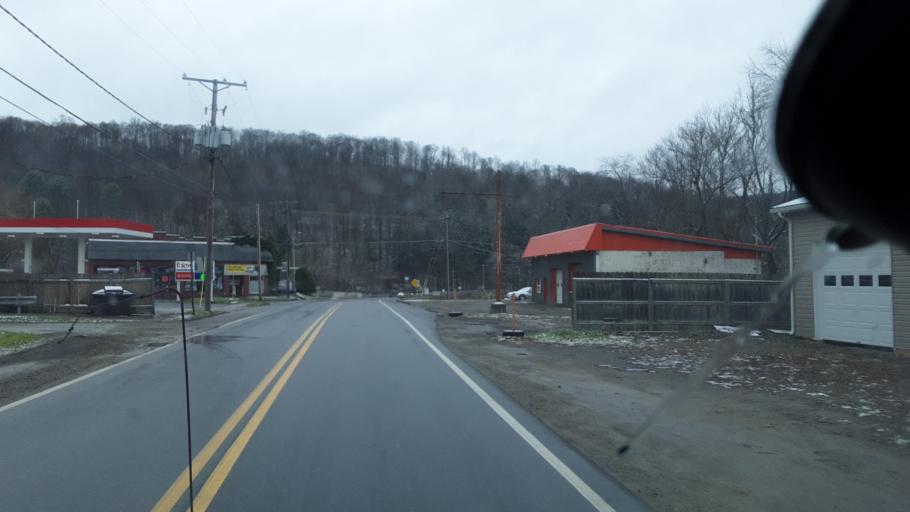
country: US
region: Pennsylvania
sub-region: Potter County
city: Shinglehouse
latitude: 41.9629
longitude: -78.1980
